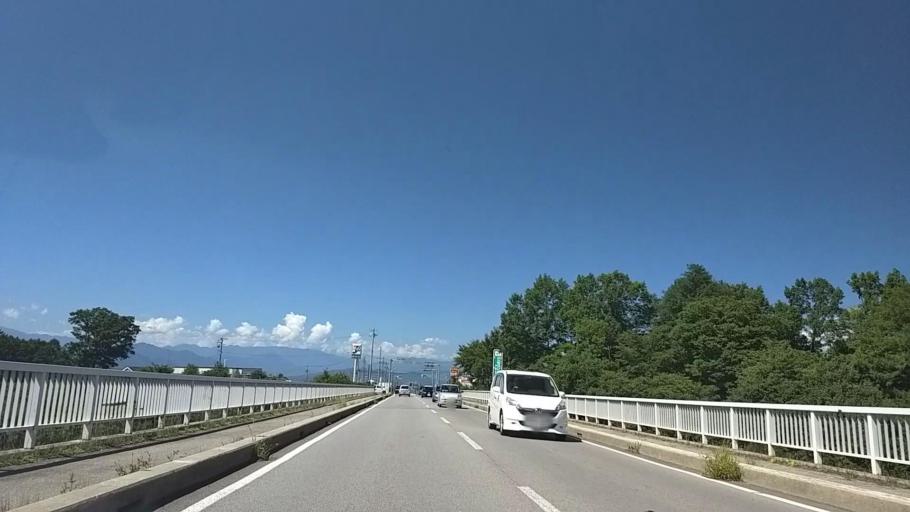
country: JP
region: Nagano
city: Komoro
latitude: 36.3515
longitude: 138.4030
